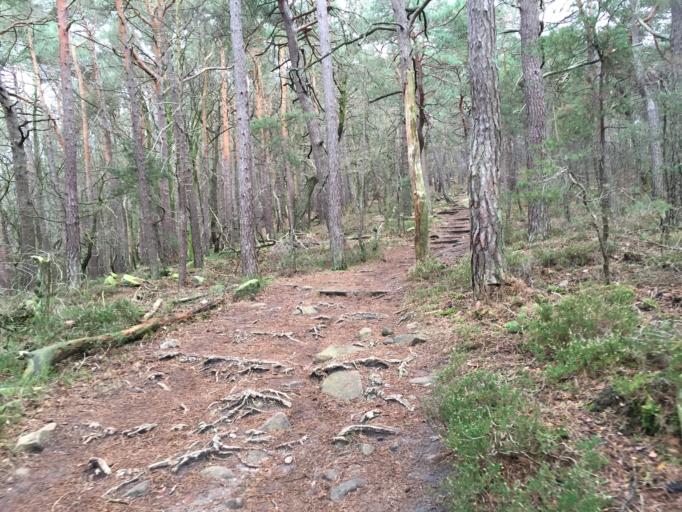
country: DE
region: Rheinland-Pfalz
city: Neustadt
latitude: 49.3365
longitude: 8.1089
